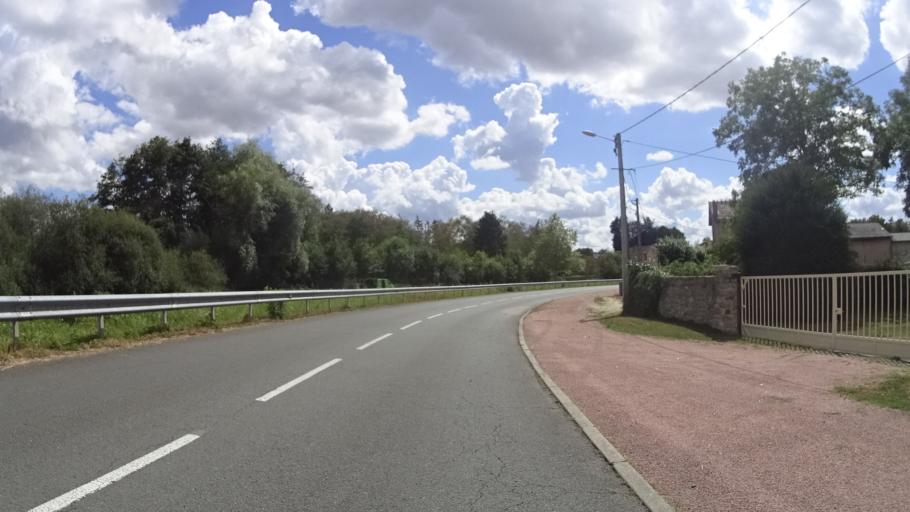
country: FR
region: Bourgogne
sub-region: Departement de Saone-et-Loire
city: Genelard
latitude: 46.5840
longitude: 4.2417
